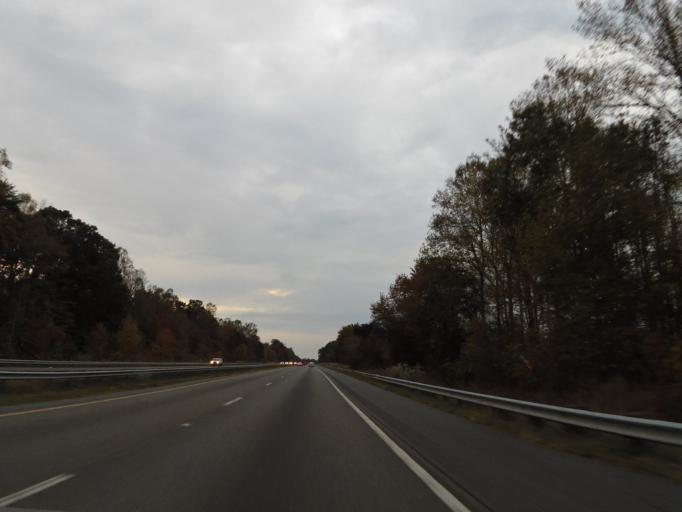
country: US
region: North Carolina
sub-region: Burke County
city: Connelly Springs
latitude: 35.7285
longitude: -81.4957
